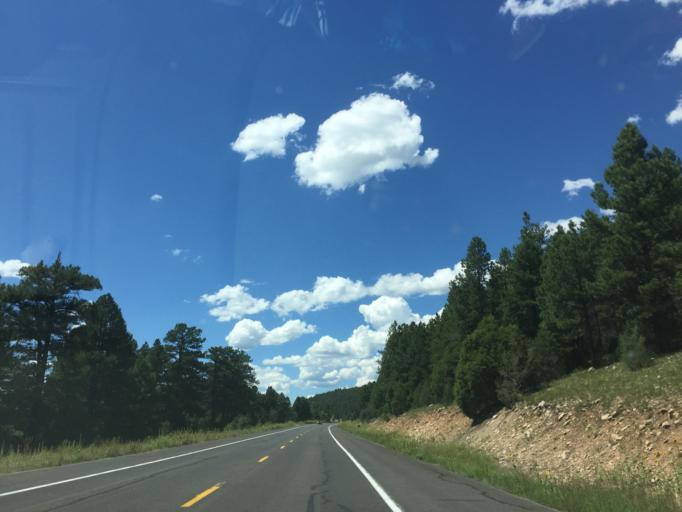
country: US
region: Arizona
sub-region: Coconino County
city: Mountainaire
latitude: 35.1005
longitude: -111.5573
